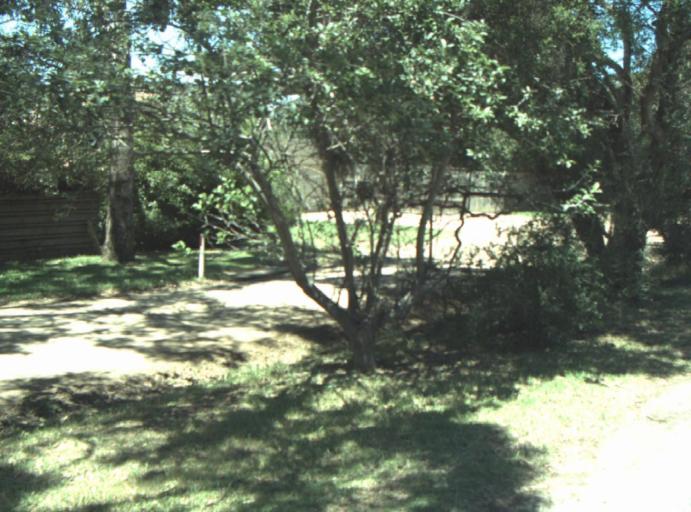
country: AU
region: Victoria
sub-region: Greater Geelong
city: Leopold
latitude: -38.2554
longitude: 144.5361
